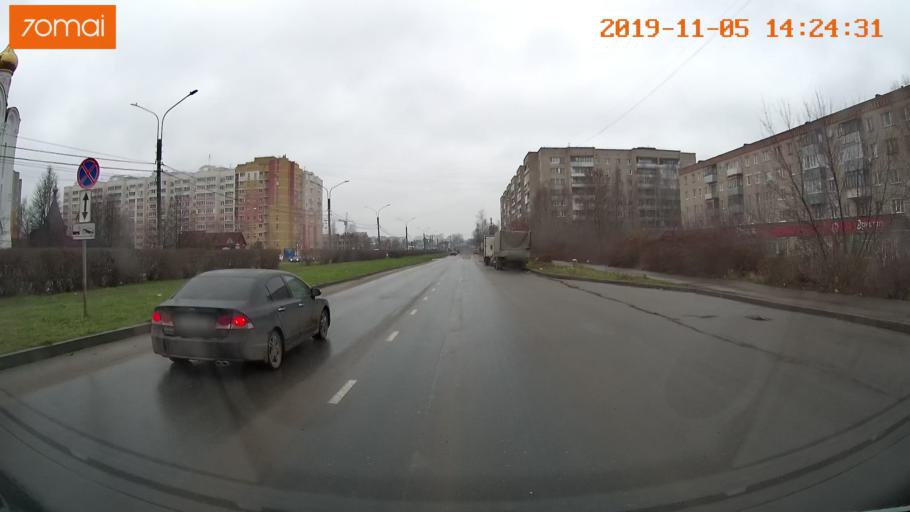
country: RU
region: Ivanovo
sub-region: Gorod Ivanovo
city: Ivanovo
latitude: 56.9687
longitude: 40.9972
